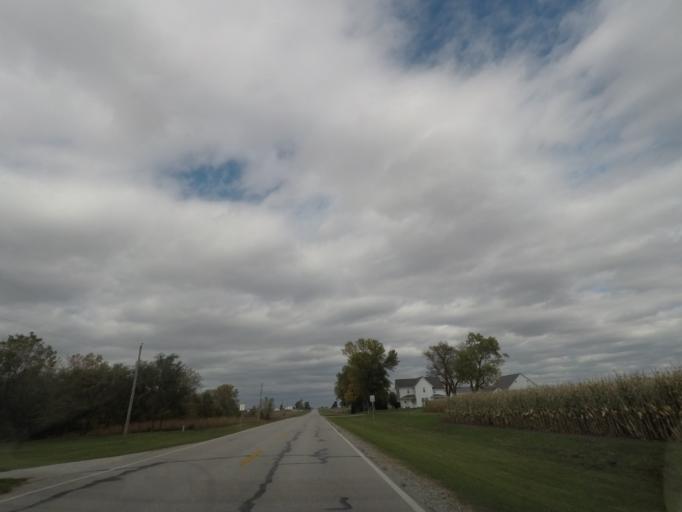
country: US
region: Iowa
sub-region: Story County
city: Huxley
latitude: 41.8417
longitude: -93.5315
